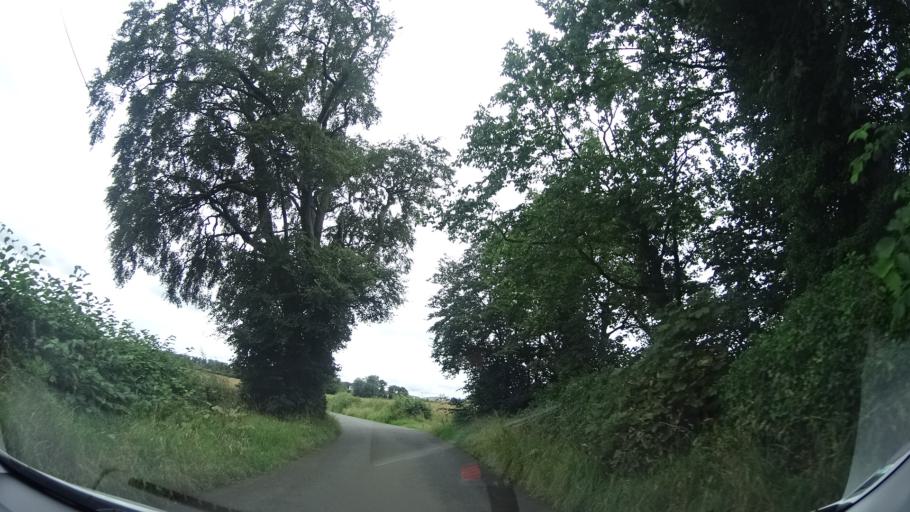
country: GB
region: Scotland
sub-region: West Lothian
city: Kirknewton
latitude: 55.9161
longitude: -3.4310
